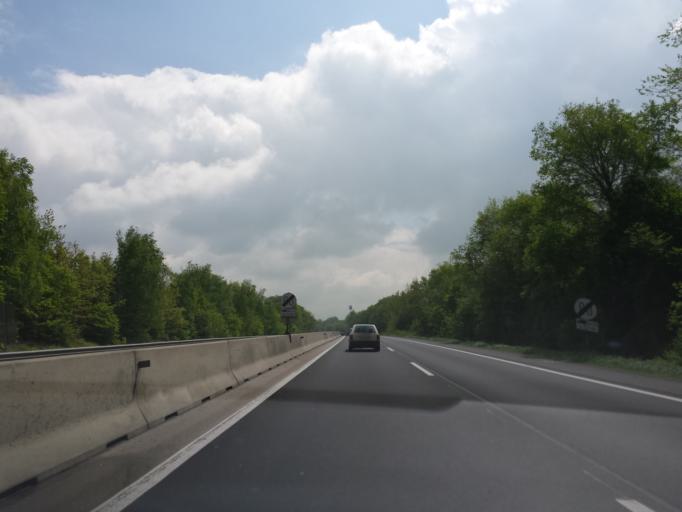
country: AT
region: Lower Austria
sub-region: Politischer Bezirk Bruck an der Leitha
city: Trautmannsdorf an der Leitha
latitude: 48.0626
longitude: 16.6999
